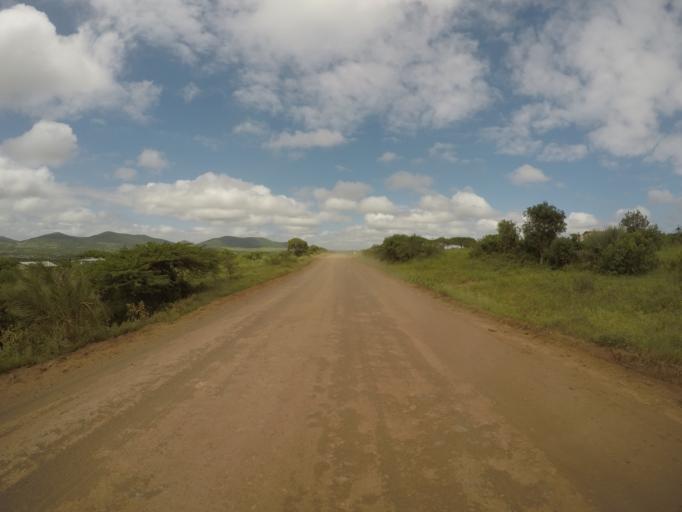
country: ZA
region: KwaZulu-Natal
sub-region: uThungulu District Municipality
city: Empangeni
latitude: -28.6061
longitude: 31.8484
